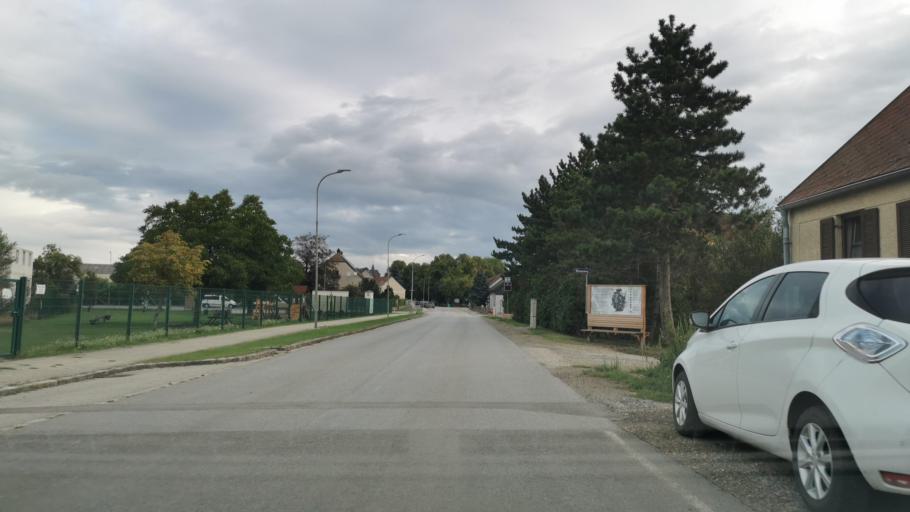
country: AT
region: Lower Austria
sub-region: Politischer Bezirk Ganserndorf
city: Glinzendorf
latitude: 48.2435
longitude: 16.6397
